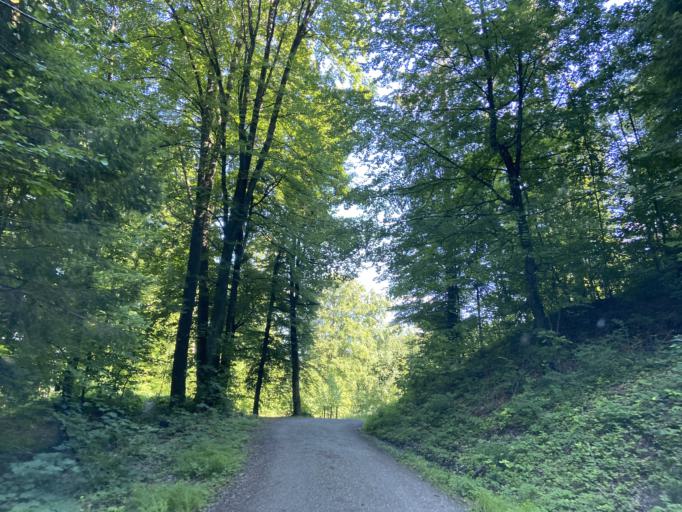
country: CH
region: Zurich
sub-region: Bezirk Winterthur
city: Wuelflingen (Kreis 6) / Niederfeld
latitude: 47.5075
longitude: 8.6655
